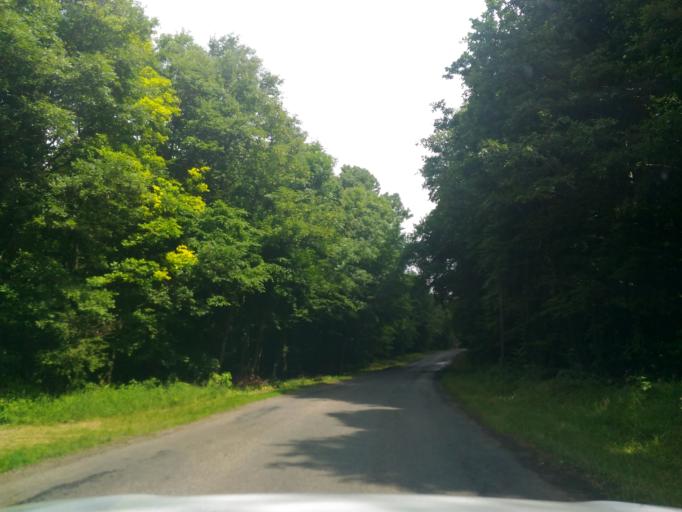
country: HU
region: Baranya
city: Pecs
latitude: 46.1294
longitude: 18.2283
